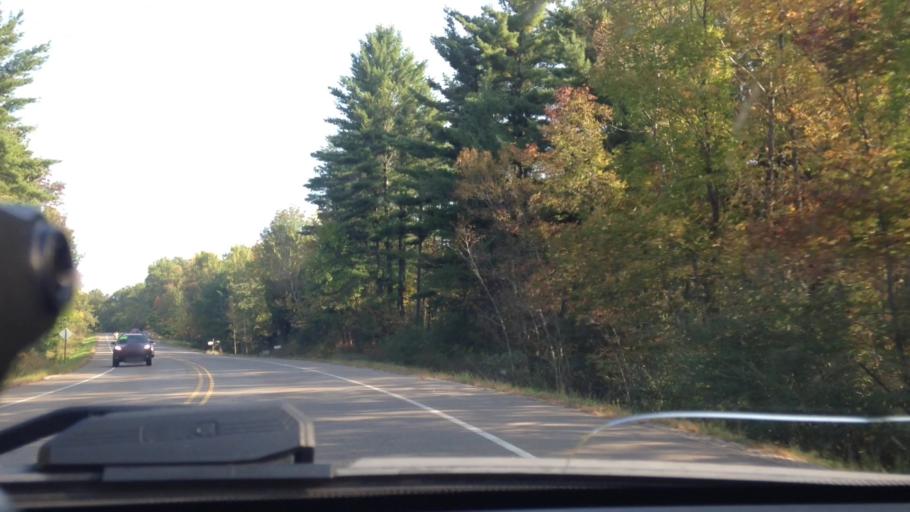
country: US
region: Michigan
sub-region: Dickinson County
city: Quinnesec
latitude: 45.8118
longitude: -87.9856
